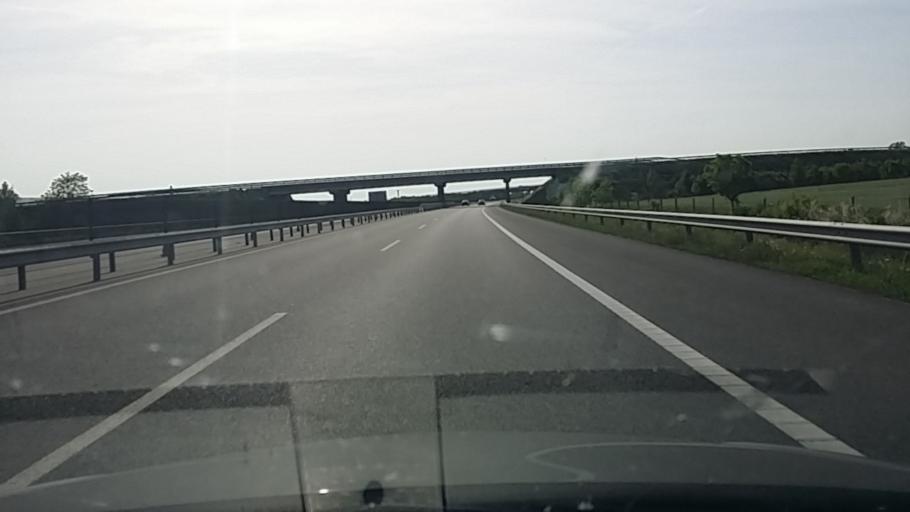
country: HU
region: Hajdu-Bihar
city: Gorbehaza
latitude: 47.7936
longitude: 21.2636
